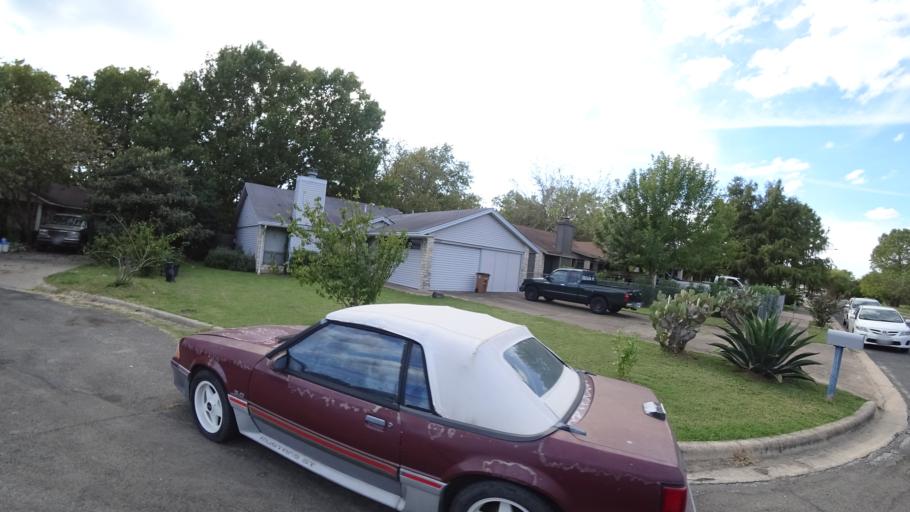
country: US
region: Texas
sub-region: Travis County
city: Onion Creek
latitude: 30.1923
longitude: -97.7523
